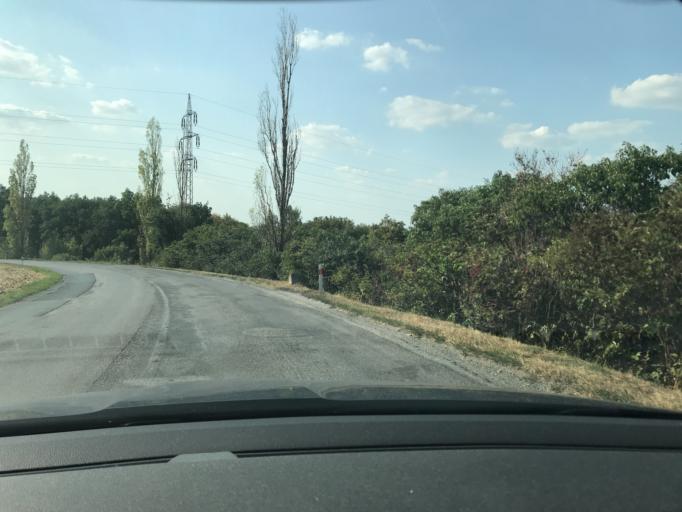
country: CZ
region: Central Bohemia
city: Kralupy nad Vltavou
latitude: 50.2165
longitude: 14.3167
